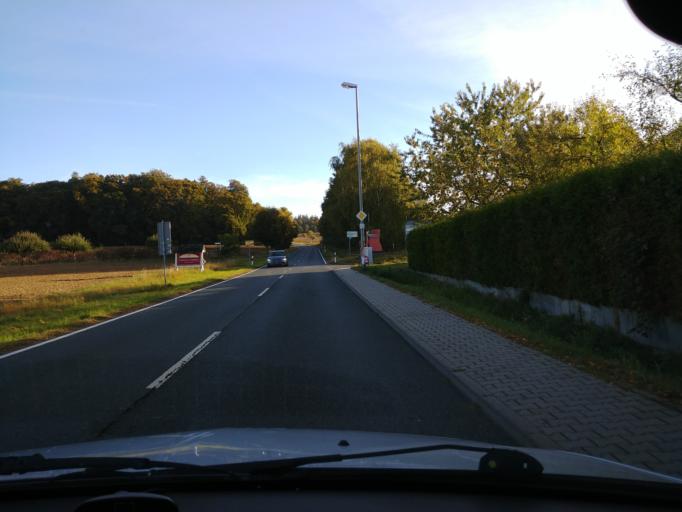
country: DE
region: Hesse
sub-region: Regierungsbezirk Darmstadt
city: Waldems
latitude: 50.2760
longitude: 8.3499
